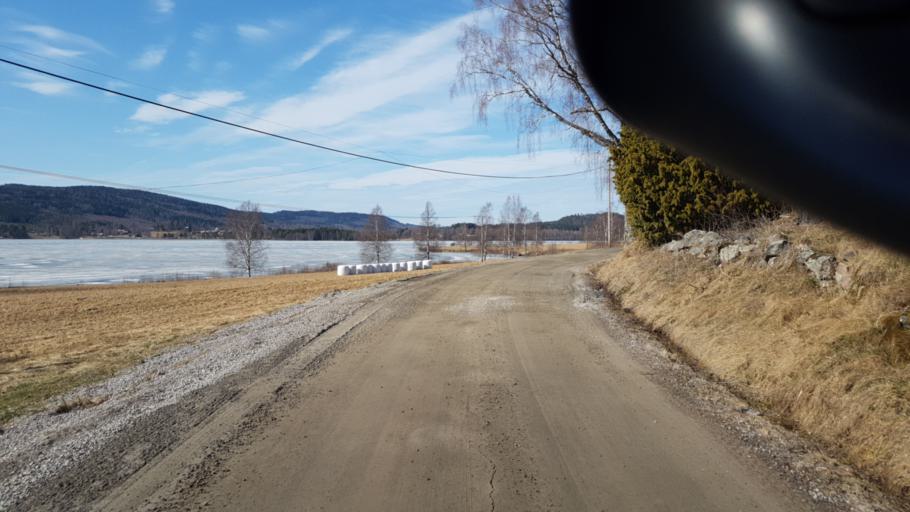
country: SE
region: Vaermland
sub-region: Arvika Kommun
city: Arvika
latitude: 59.7300
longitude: 12.8335
